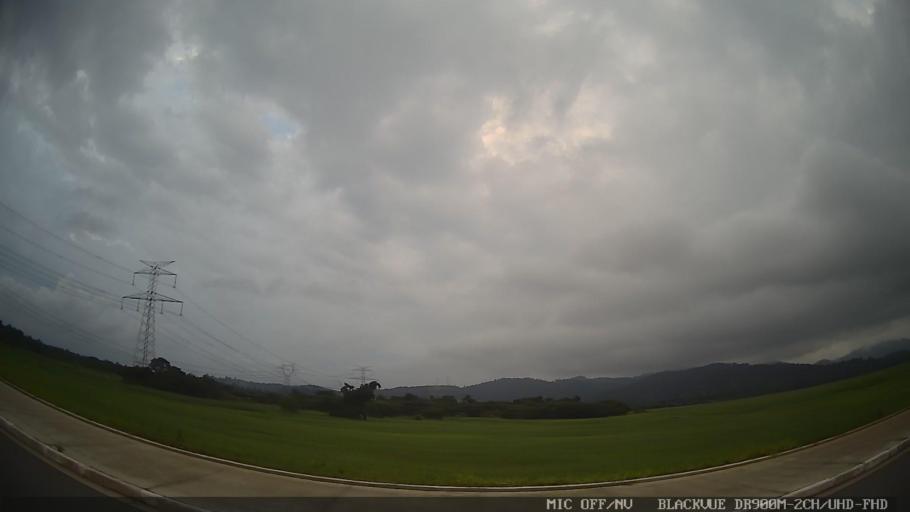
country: BR
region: Sao Paulo
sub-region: Mogi das Cruzes
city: Mogi das Cruzes
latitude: -23.5412
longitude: -46.2449
